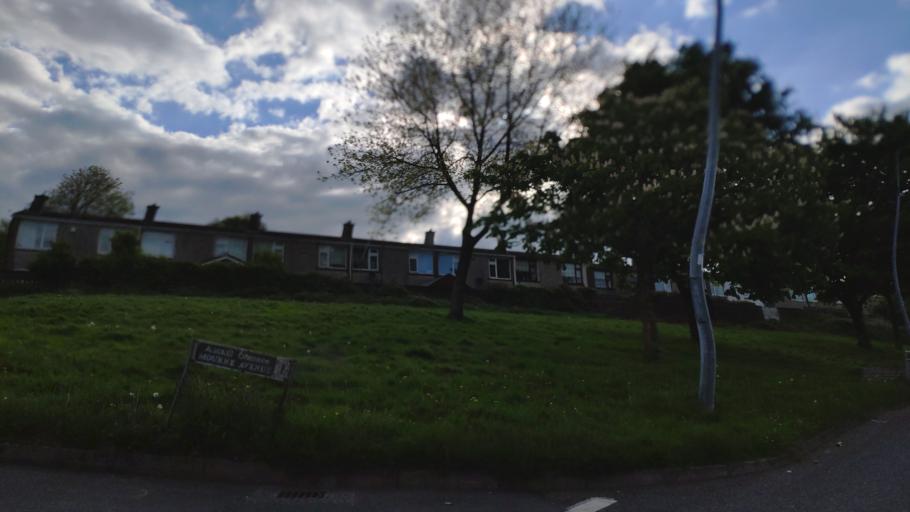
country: IE
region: Munster
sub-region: County Cork
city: Cork
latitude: 51.9103
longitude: -8.4576
